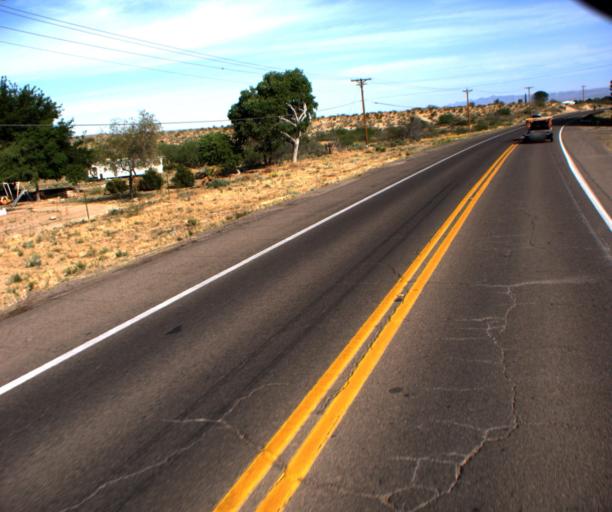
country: US
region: Arizona
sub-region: Graham County
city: Swift Trail Junction
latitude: 32.7327
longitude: -109.7156
